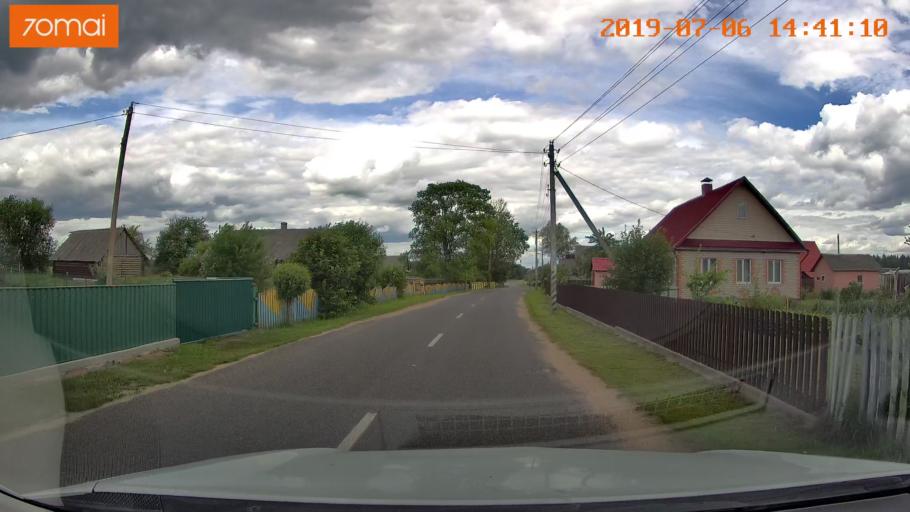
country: BY
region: Minsk
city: Ivyanyets
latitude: 53.9299
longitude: 26.6751
